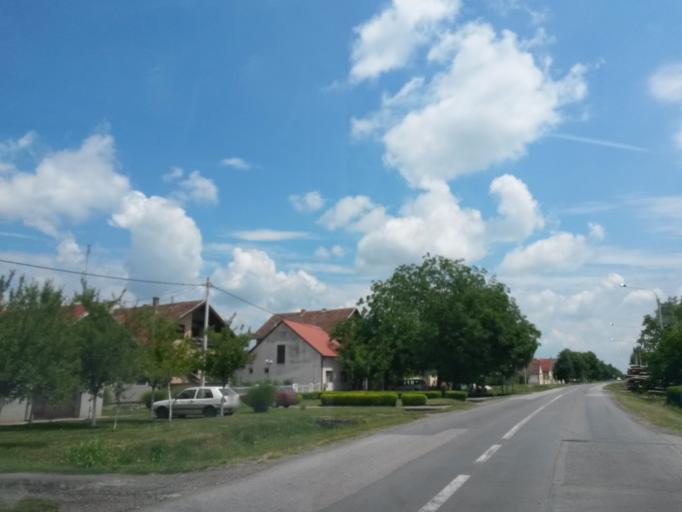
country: HR
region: Osjecko-Baranjska
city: Sarvas
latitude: 45.5189
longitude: 18.8635
